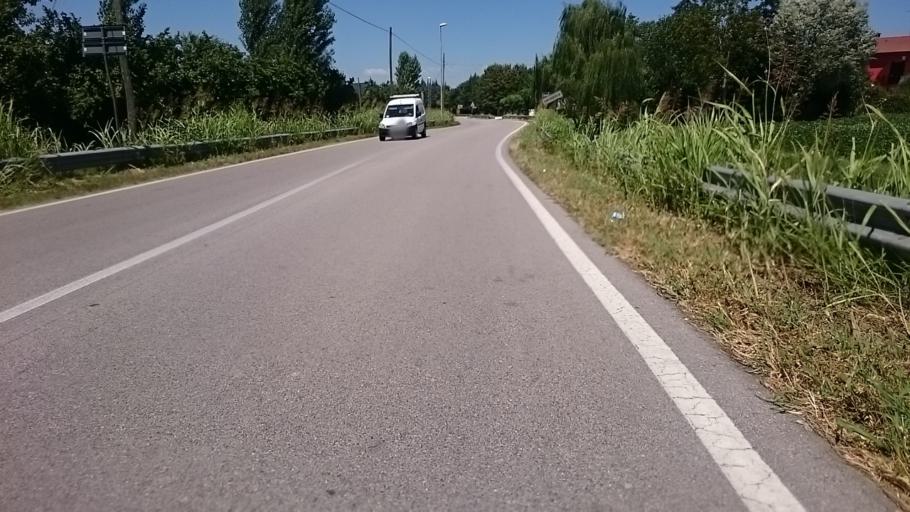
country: IT
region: Veneto
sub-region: Provincia di Padova
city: Campodarsego
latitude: 45.5123
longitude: 11.9326
